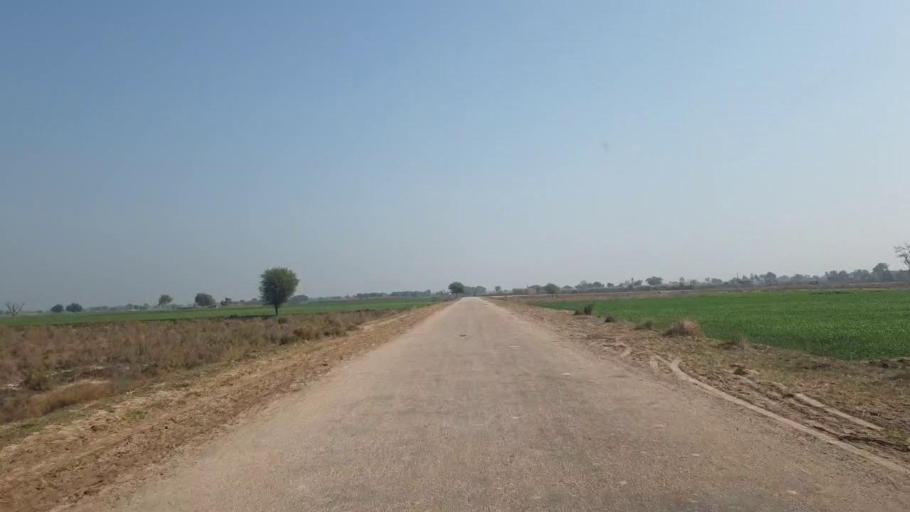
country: PK
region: Sindh
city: Sakrand
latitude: 26.0413
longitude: 68.4345
